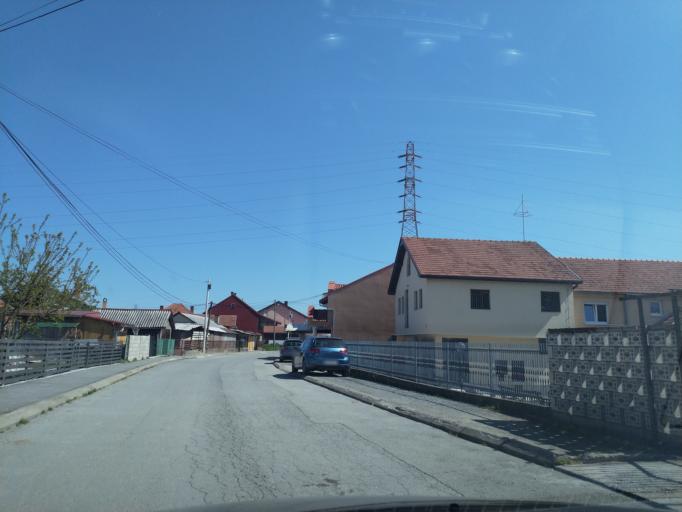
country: RS
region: Central Serbia
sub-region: Kolubarski Okrug
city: Valjevo
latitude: 44.2797
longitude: 19.8682
